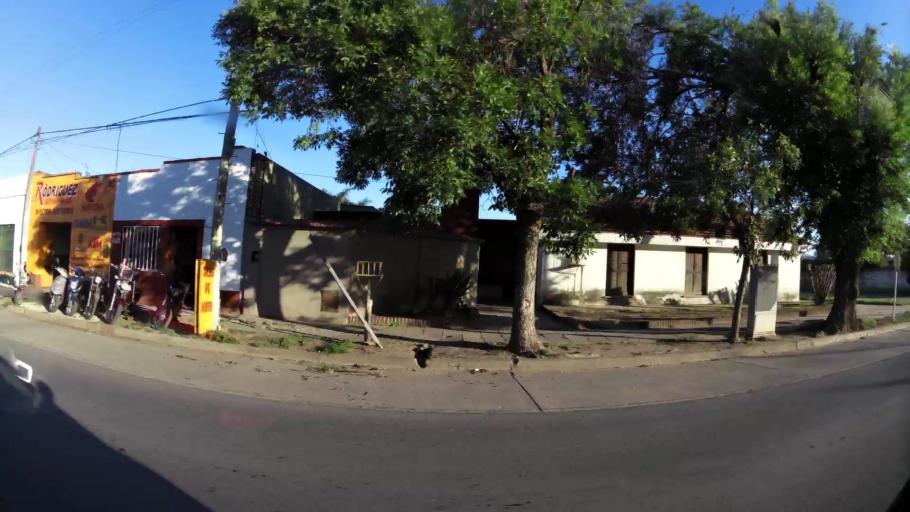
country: AR
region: Cordoba
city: Las Varillas
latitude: -31.8781
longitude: -62.7206
